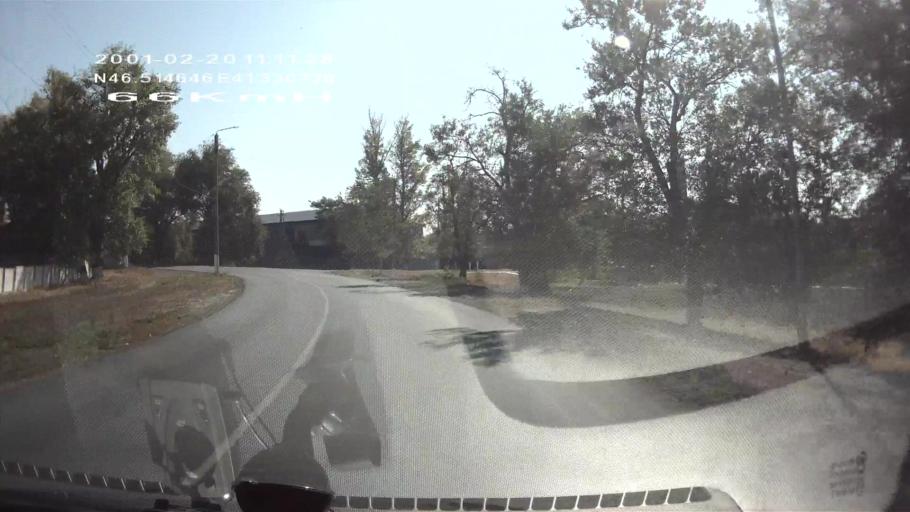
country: RU
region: Rostov
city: Gigant
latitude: 46.5145
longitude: 41.3308
